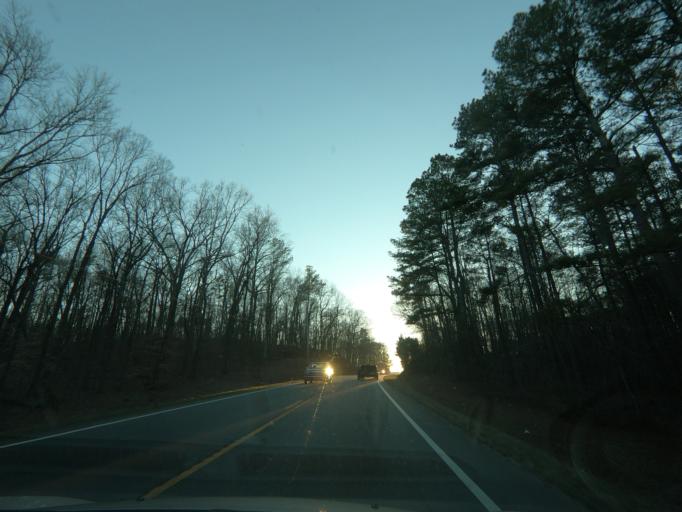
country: US
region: Georgia
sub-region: Forsyth County
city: Cumming
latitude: 34.3032
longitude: -84.2210
